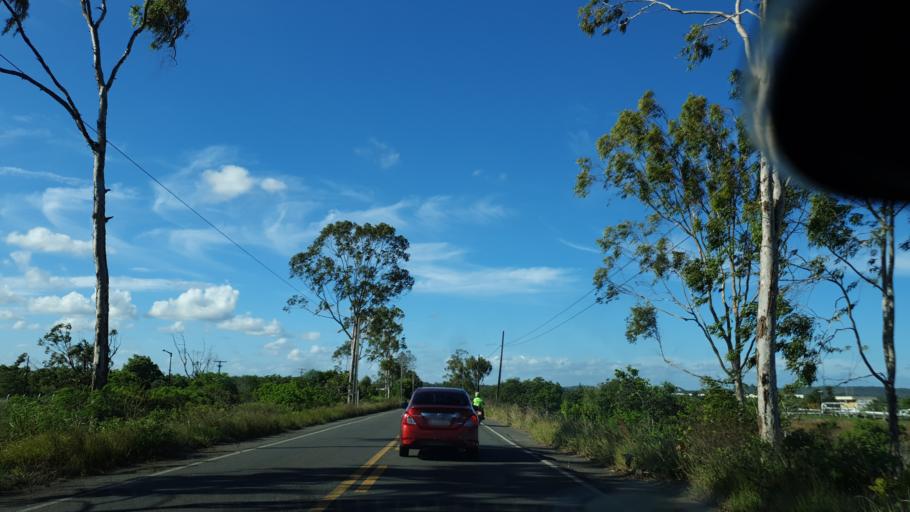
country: BR
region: Bahia
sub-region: Camacari
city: Camacari
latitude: -12.6543
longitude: -38.3029
